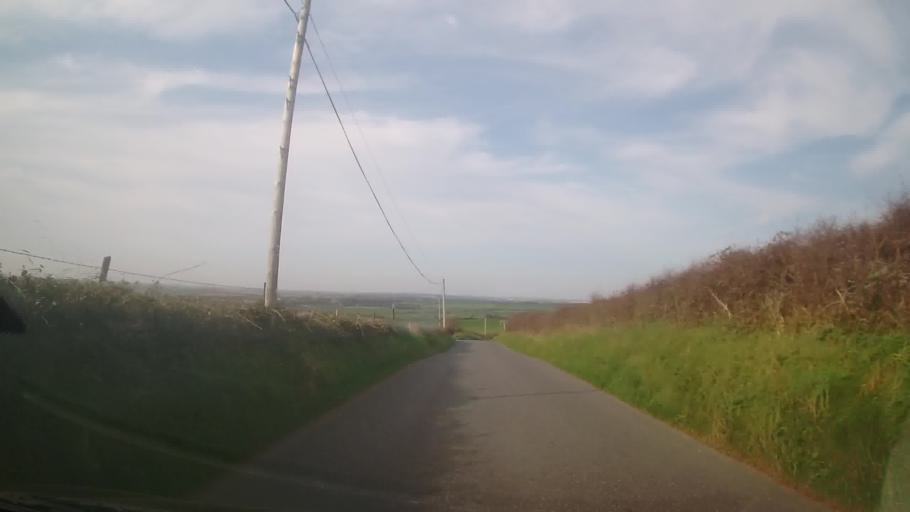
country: GB
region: Wales
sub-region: Pembrokeshire
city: Camrose
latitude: 51.8617
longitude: -5.0532
